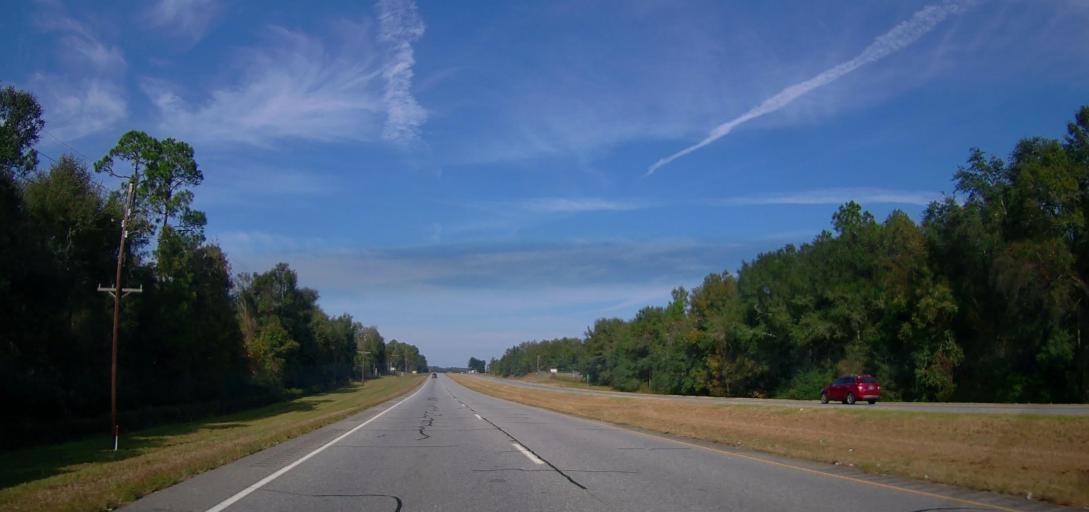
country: US
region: Georgia
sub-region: Mitchell County
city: Camilla
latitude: 31.3191
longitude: -84.1740
